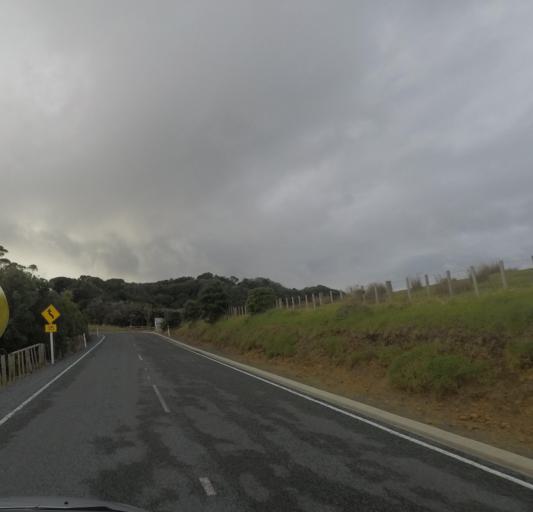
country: NZ
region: Auckland
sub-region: Auckland
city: Warkworth
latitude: -36.3769
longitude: 174.8134
